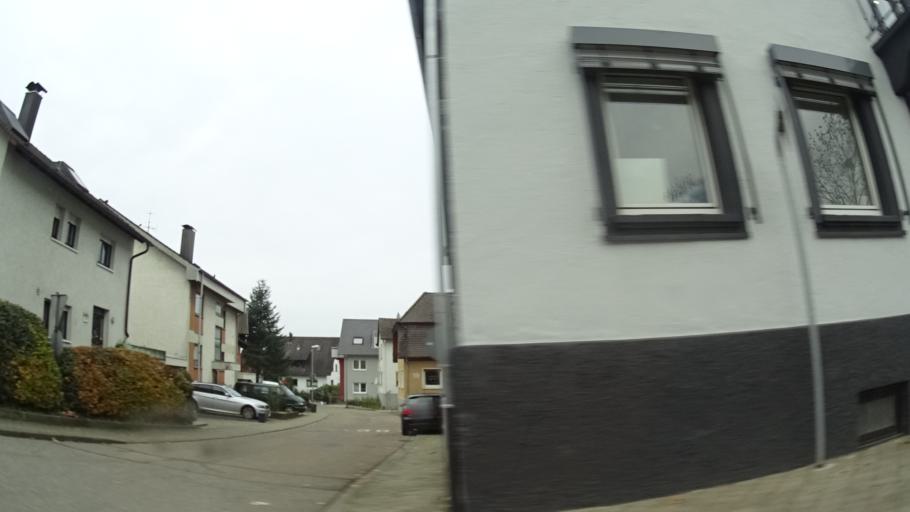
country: DE
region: Baden-Wuerttemberg
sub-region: Karlsruhe Region
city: Sinzheim
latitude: 48.7590
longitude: 8.1683
